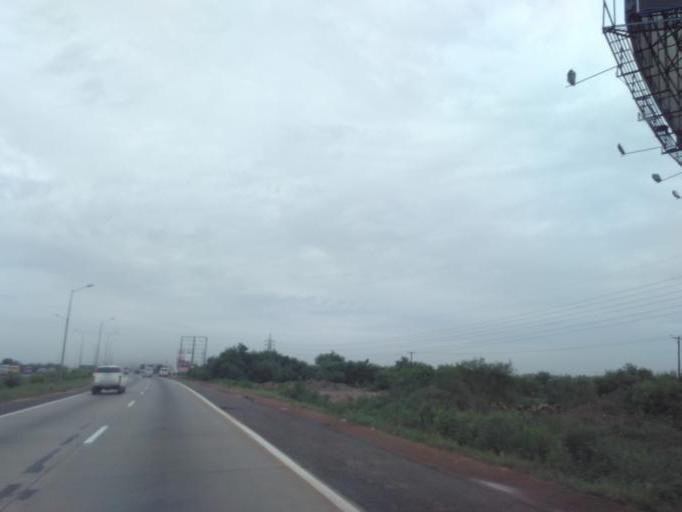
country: GH
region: Greater Accra
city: Nungua
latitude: 5.6600
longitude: -0.0773
